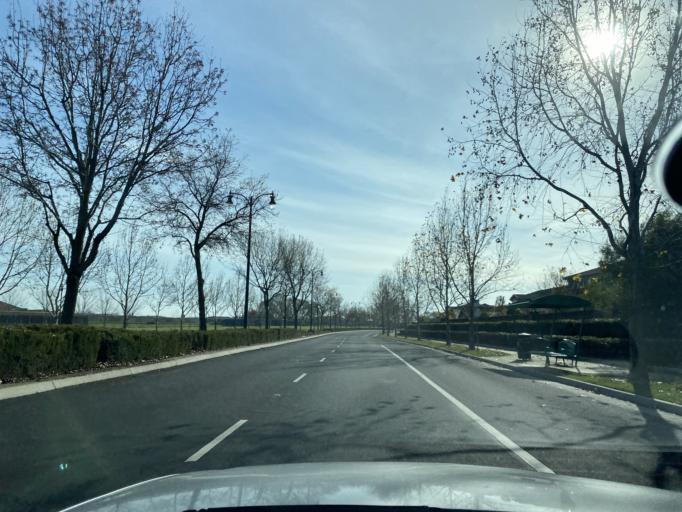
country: US
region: California
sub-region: Sacramento County
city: Laguna
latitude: 38.4003
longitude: -121.4017
